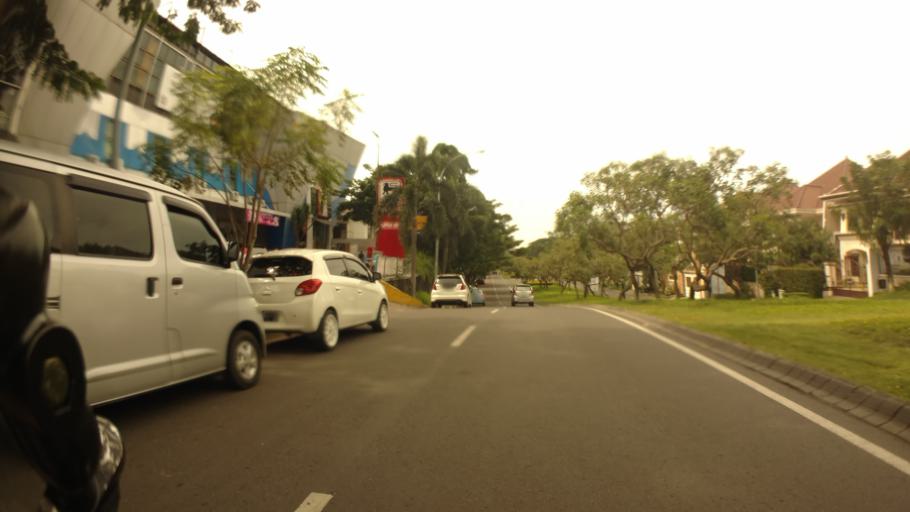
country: ID
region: East Java
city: Driyorejo
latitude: -7.2915
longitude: 112.6482
